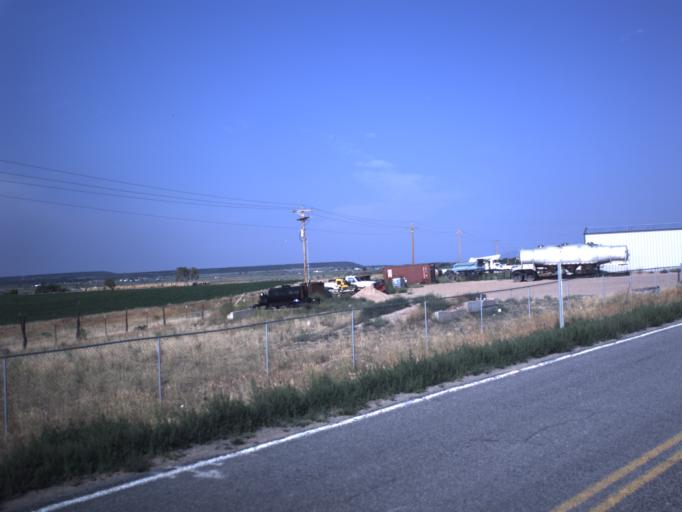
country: US
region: Utah
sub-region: Duchesne County
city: Duchesne
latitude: 40.3558
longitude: -110.3847
